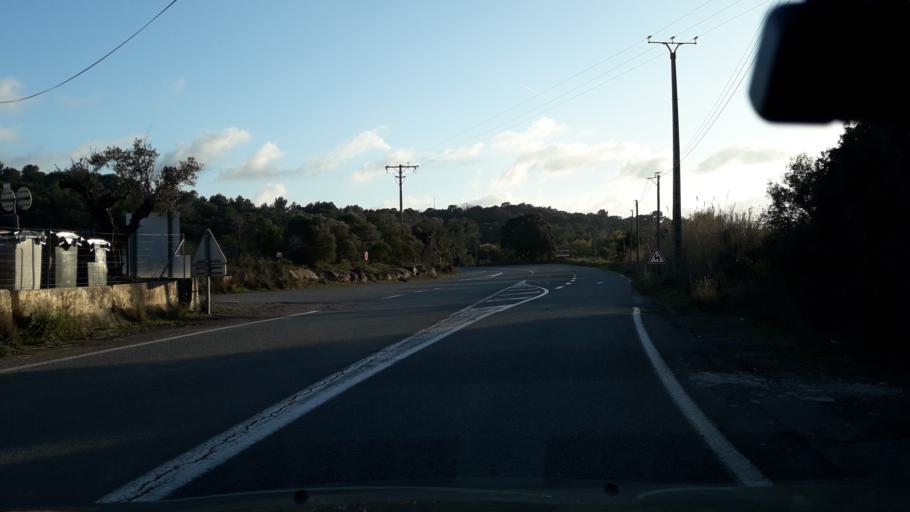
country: FR
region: Provence-Alpes-Cote d'Azur
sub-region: Departement du Var
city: Saint-Raphael
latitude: 43.4744
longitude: 6.7698
